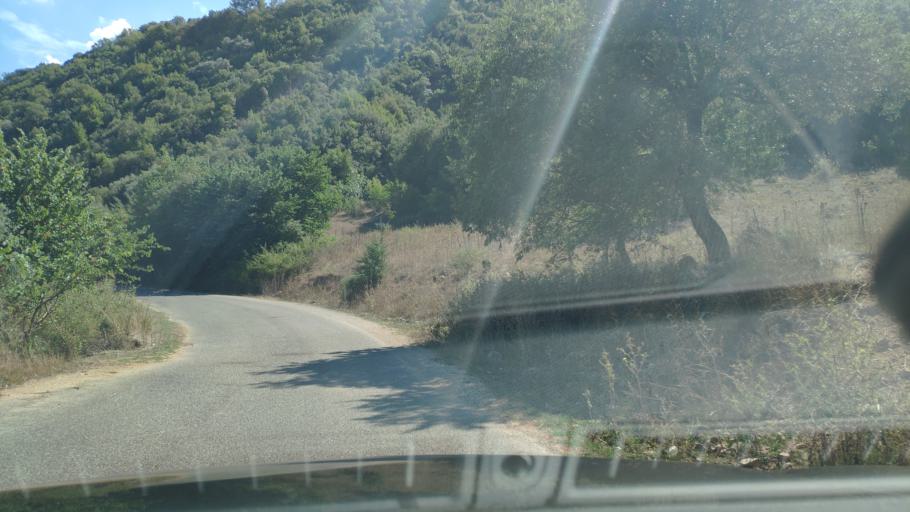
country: GR
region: West Greece
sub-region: Nomos Aitolias kai Akarnanias
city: Katouna
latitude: 38.8304
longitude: 21.0989
